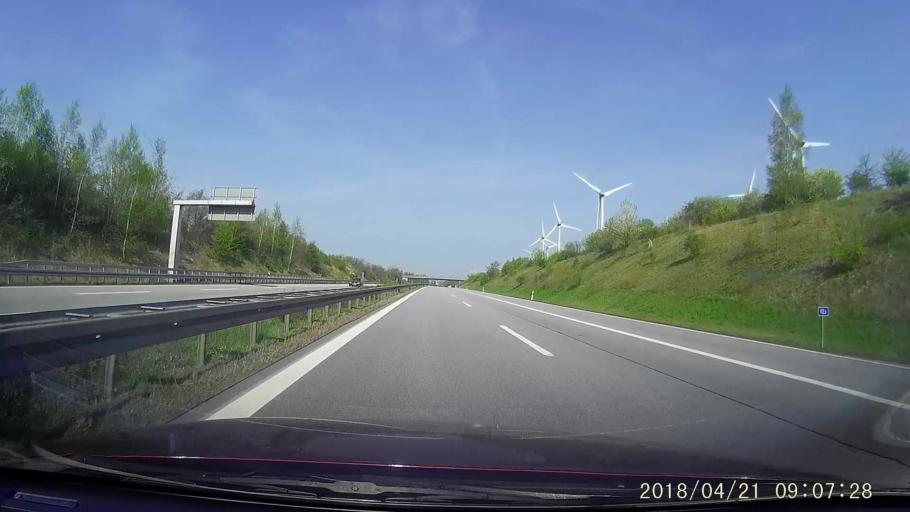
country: DE
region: Saxony
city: Goerlitz
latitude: 51.1993
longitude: 14.9600
